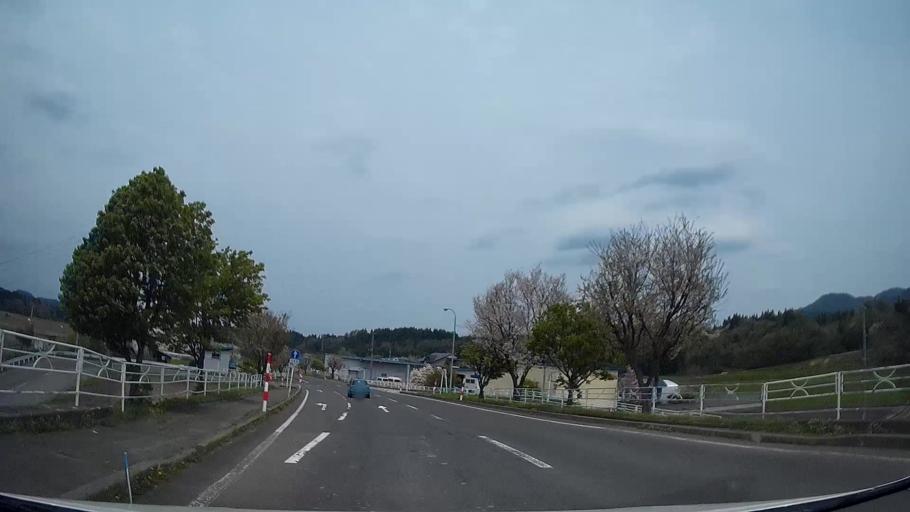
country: JP
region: Akita
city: Hanawa
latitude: 40.1578
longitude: 140.7941
